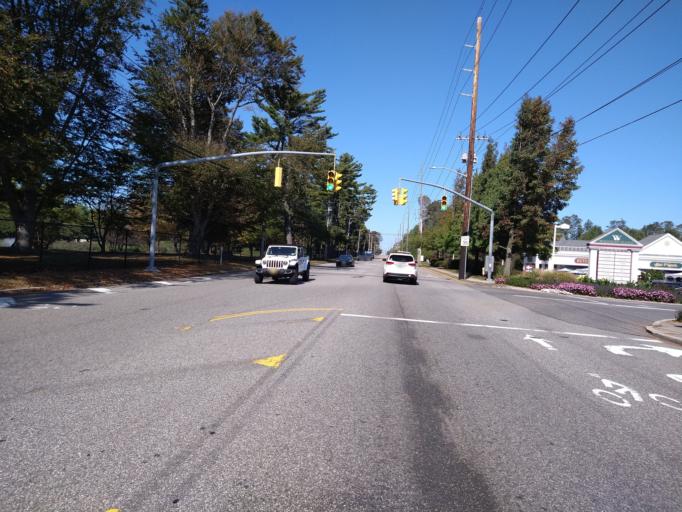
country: US
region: New York
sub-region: Nassau County
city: Woodbury
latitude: 40.8156
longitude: -73.4776
